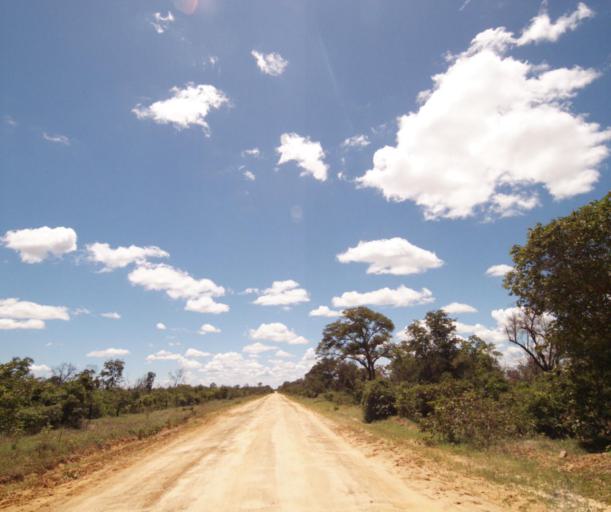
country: BR
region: Bahia
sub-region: Carinhanha
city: Carinhanha
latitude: -14.2090
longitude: -43.9962
